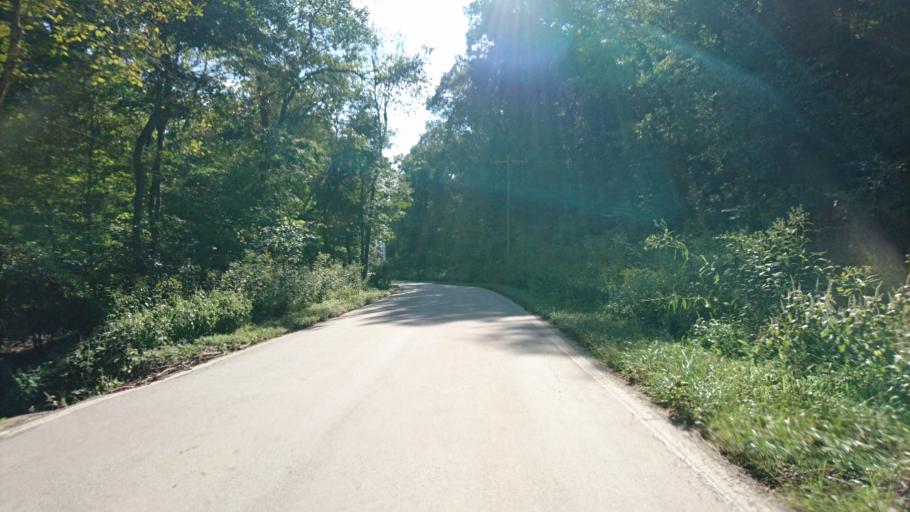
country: US
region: Missouri
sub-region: Saint Louis County
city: Wildwood
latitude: 38.5632
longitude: -90.6381
